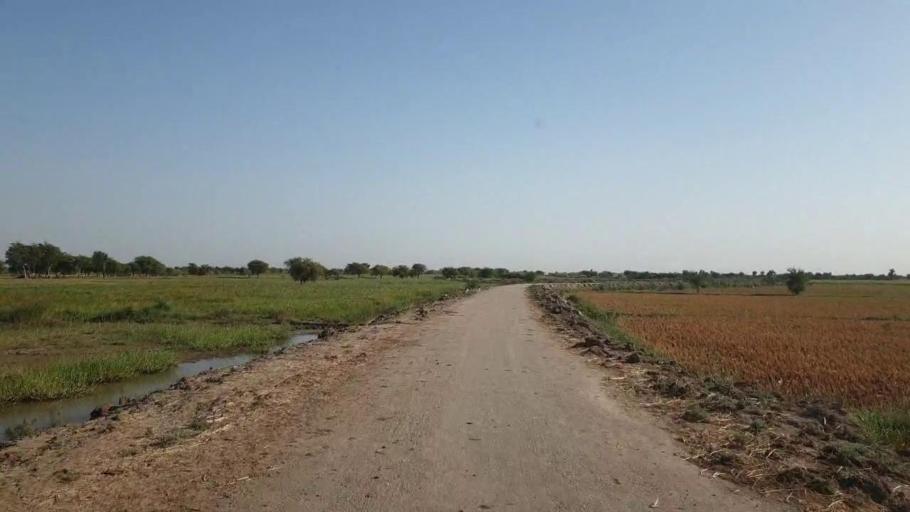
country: PK
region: Sindh
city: Badin
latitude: 24.5975
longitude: 68.9108
